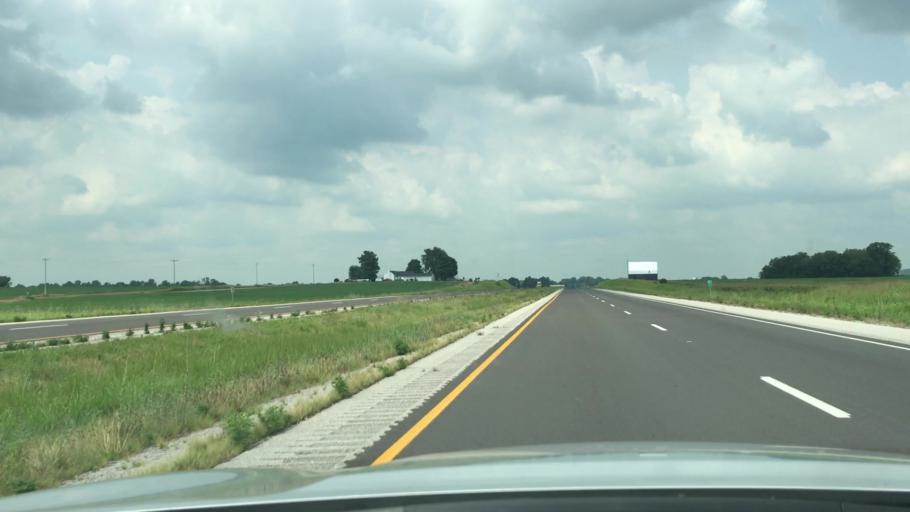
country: US
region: Kentucky
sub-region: Todd County
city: Elkton
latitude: 36.8100
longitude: -87.0409
